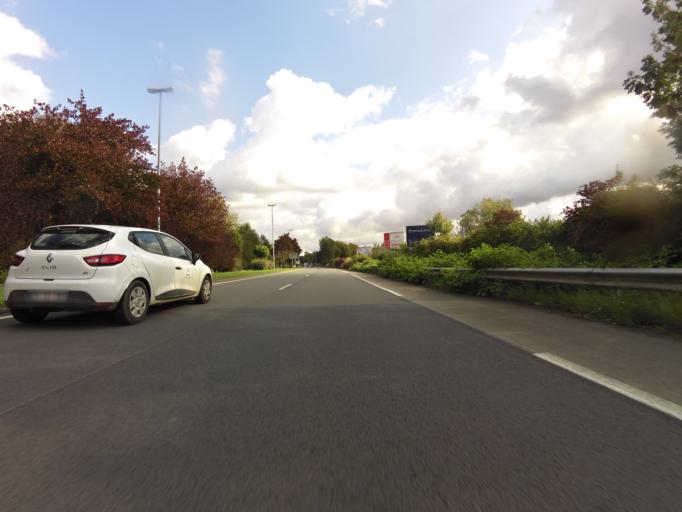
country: FR
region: Nord-Pas-de-Calais
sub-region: Departement du Nord
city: Proville
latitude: 50.1750
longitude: 3.2118
